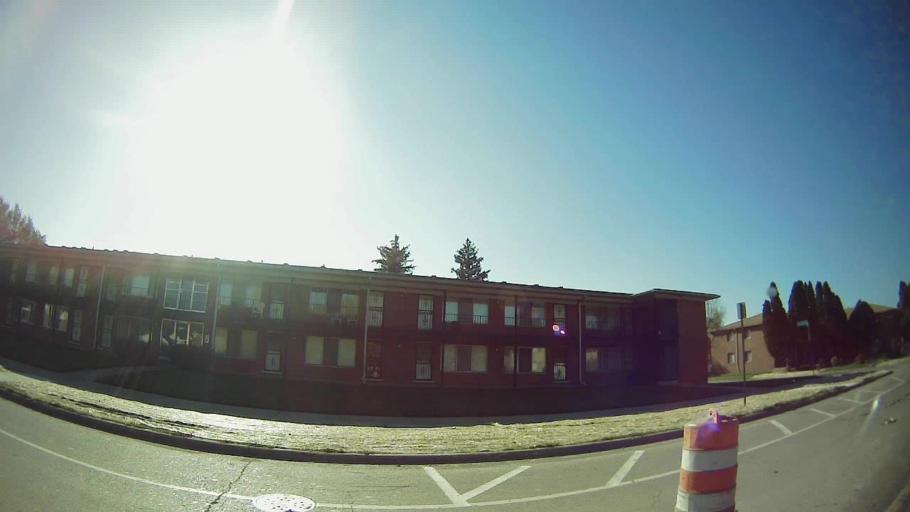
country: US
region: Michigan
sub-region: Wayne County
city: Dearborn
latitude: 42.3584
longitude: -83.1892
